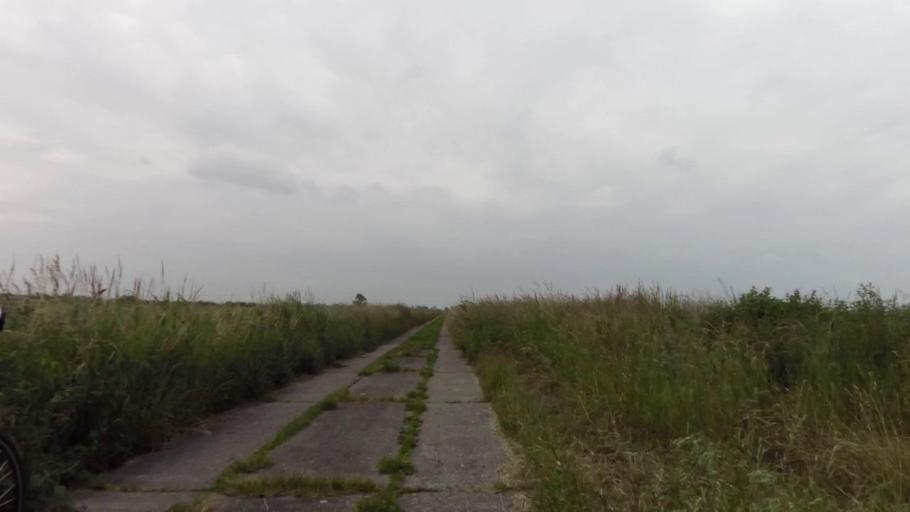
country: PL
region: West Pomeranian Voivodeship
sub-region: Powiat goleniowski
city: Stepnica
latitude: 53.5696
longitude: 14.6958
